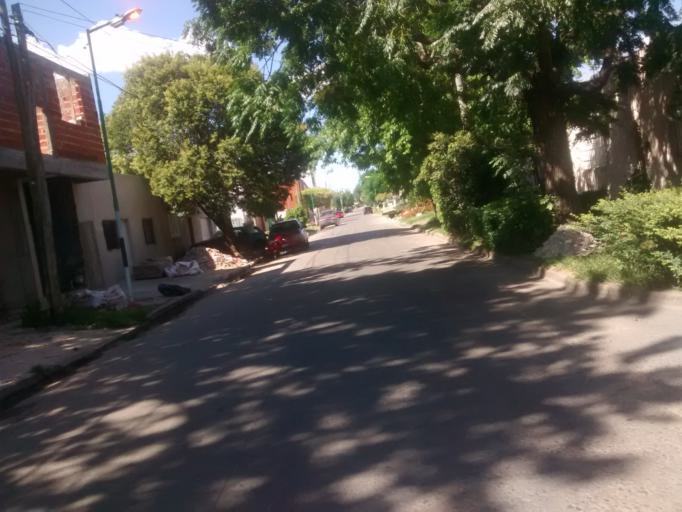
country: AR
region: Buenos Aires
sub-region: Partido de La Plata
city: La Plata
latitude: -34.9337
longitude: -57.9133
